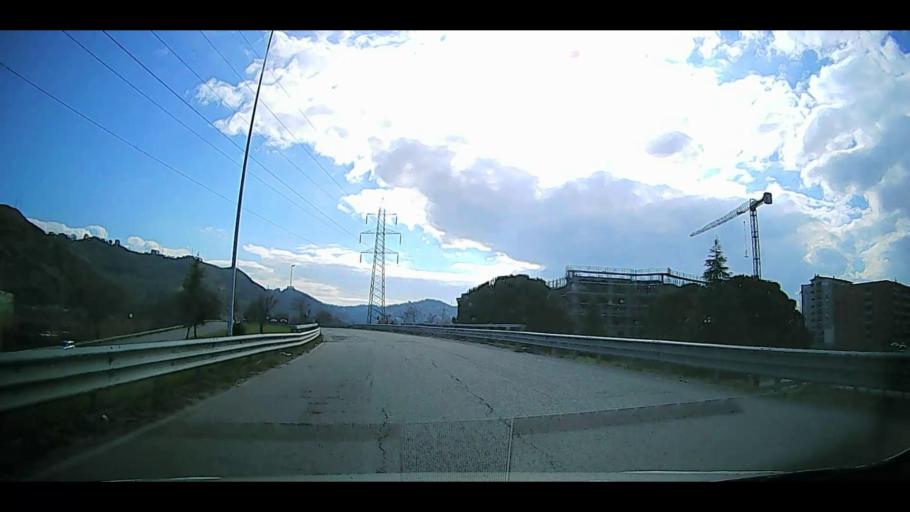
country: IT
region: Calabria
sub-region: Provincia di Cosenza
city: Cosenza
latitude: 39.3143
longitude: 16.2585
